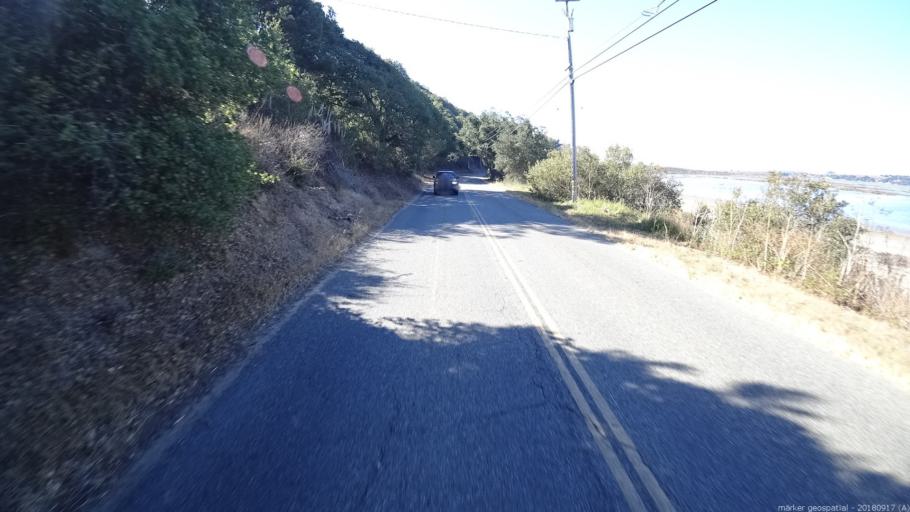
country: US
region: California
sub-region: Monterey County
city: Elkhorn
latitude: 36.8344
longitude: -121.7328
